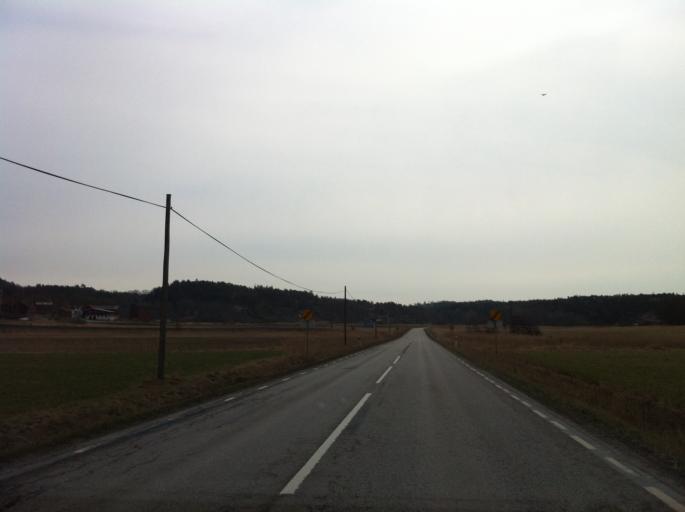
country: SE
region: Vaestra Goetaland
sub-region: Orust
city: Henan
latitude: 58.3026
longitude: 11.6997
